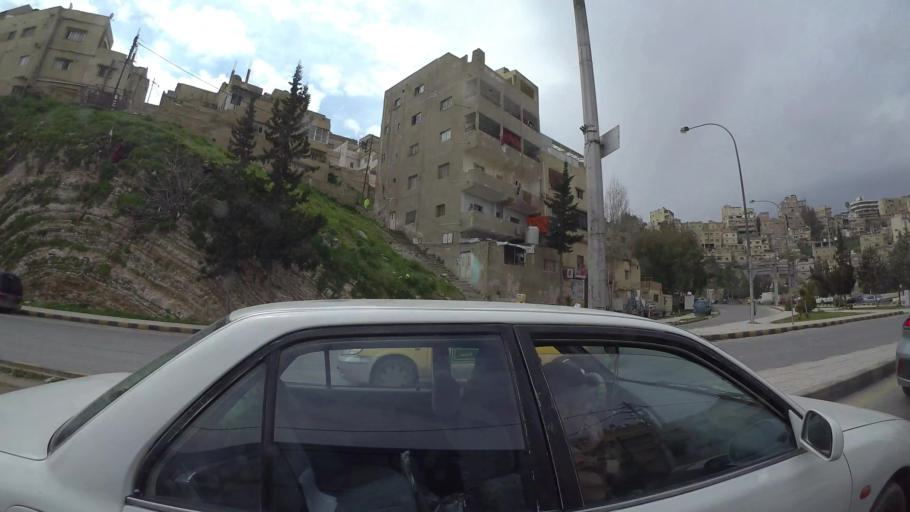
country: JO
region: Amman
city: Amman
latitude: 31.9575
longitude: 35.9358
